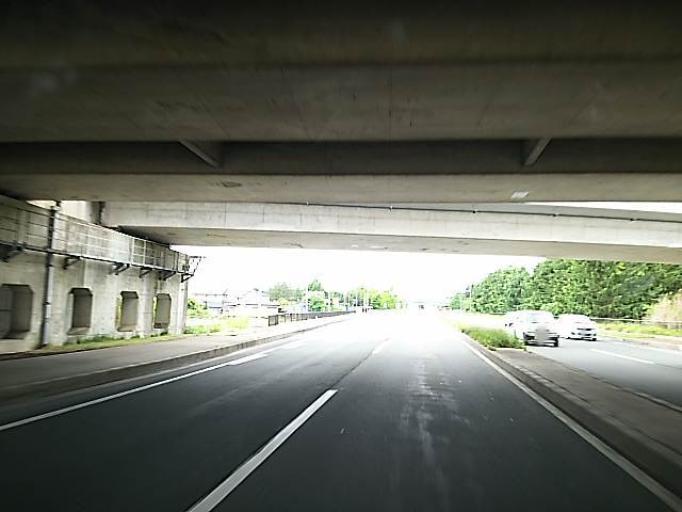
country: JP
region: Iwate
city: Morioka-shi
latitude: 39.7096
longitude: 141.0961
